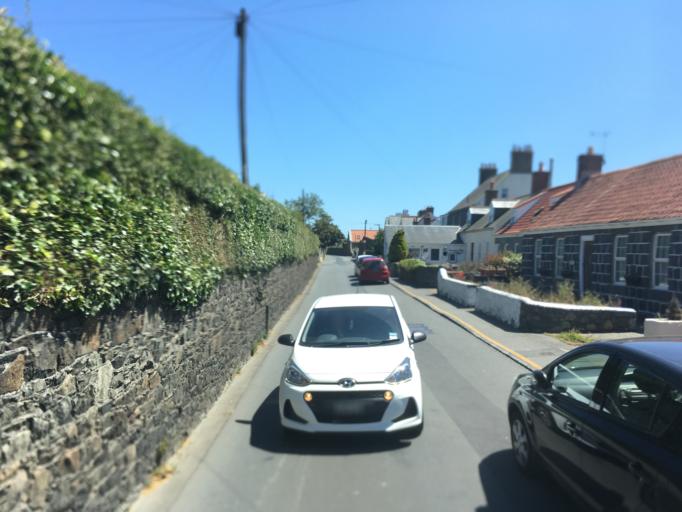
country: GG
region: St Peter Port
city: Saint Peter Port
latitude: 49.4867
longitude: -2.5184
